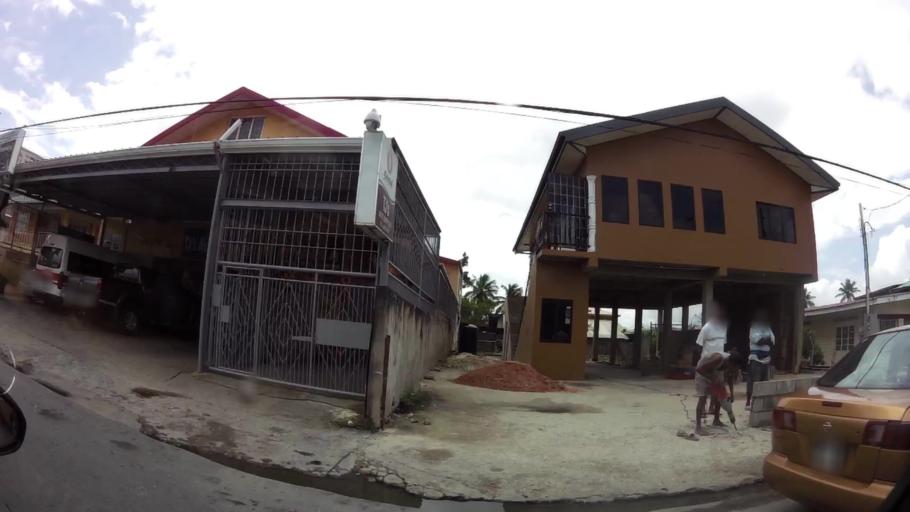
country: TT
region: Tunapuna/Piarco
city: Arouca
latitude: 10.6314
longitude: -61.3238
